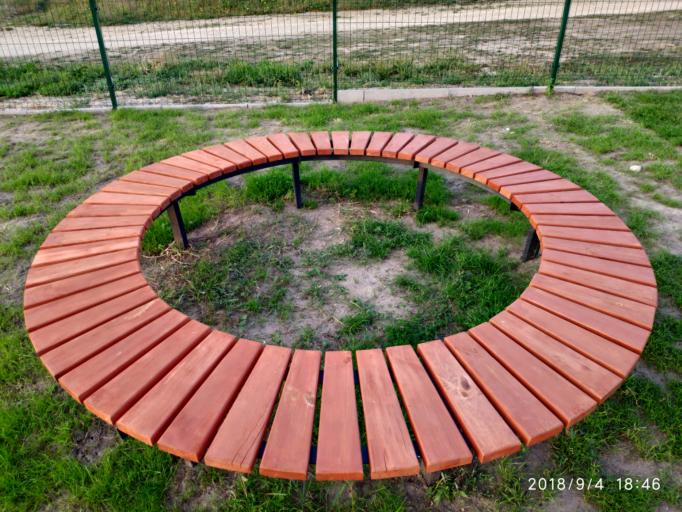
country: PL
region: Lubusz
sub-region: Zielona Gora
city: Zielona Gora
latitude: 51.9706
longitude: 15.5359
